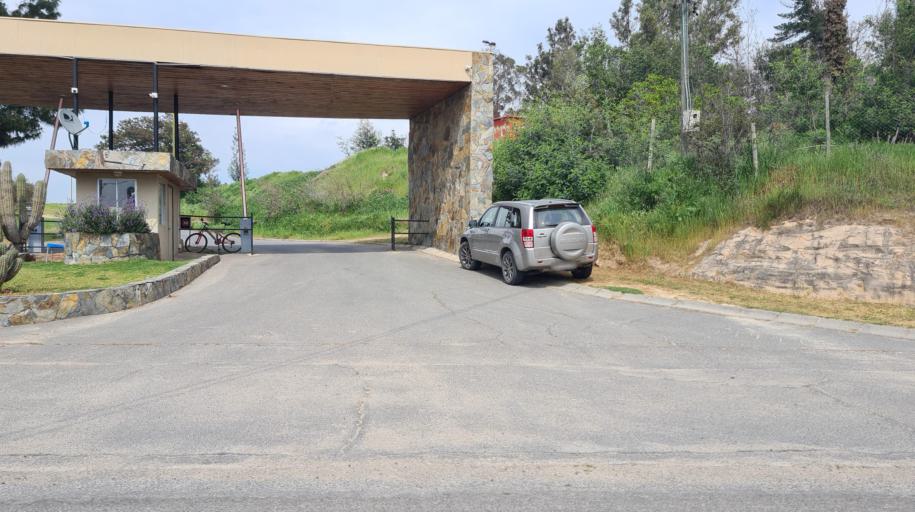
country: CL
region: O'Higgins
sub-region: Provincia de Cachapoal
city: San Vicente
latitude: -34.1514
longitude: -71.4534
